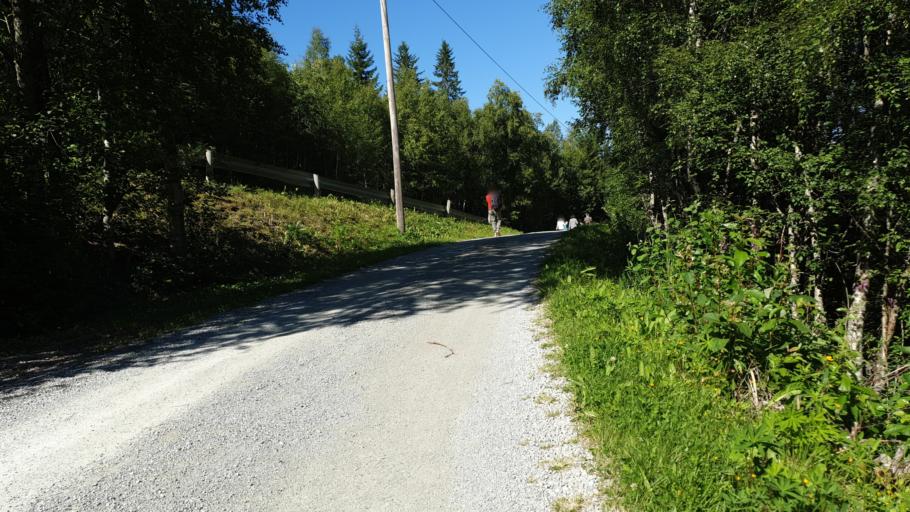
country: NO
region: Sor-Trondelag
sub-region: Meldal
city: Meldal
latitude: 63.1232
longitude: 9.7017
